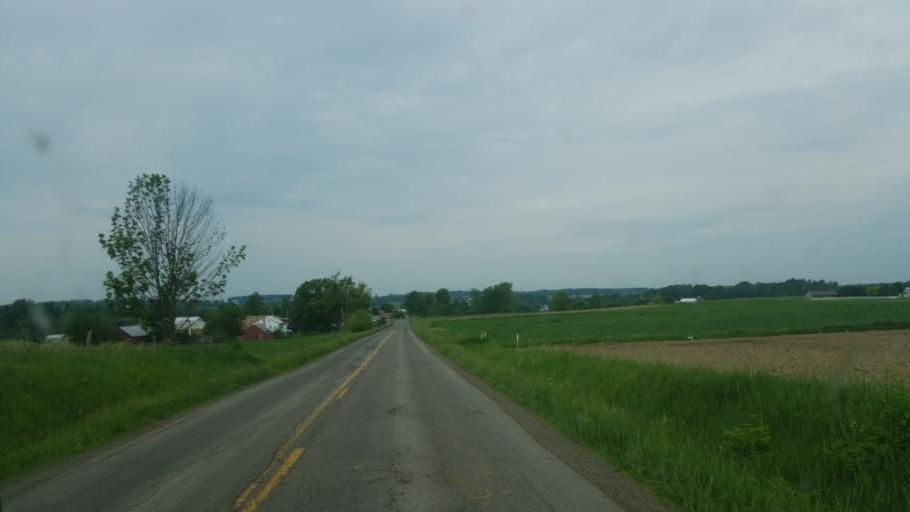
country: US
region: Ohio
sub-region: Wayne County
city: Dalton
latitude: 40.6957
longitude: -81.7305
